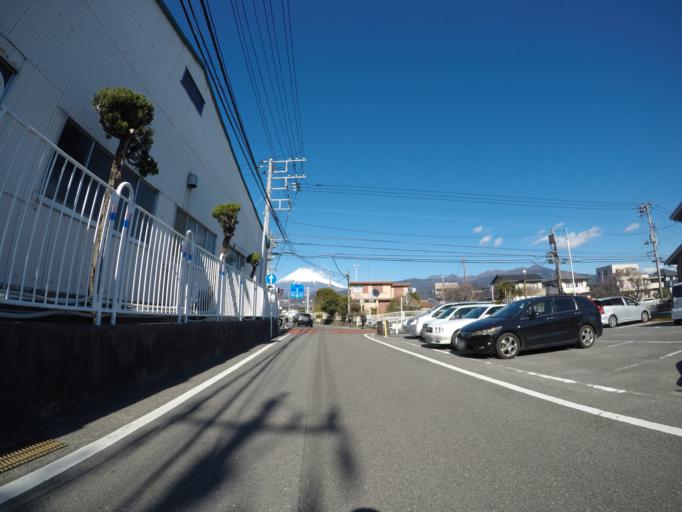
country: JP
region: Shizuoka
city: Fuji
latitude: 35.1377
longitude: 138.7418
